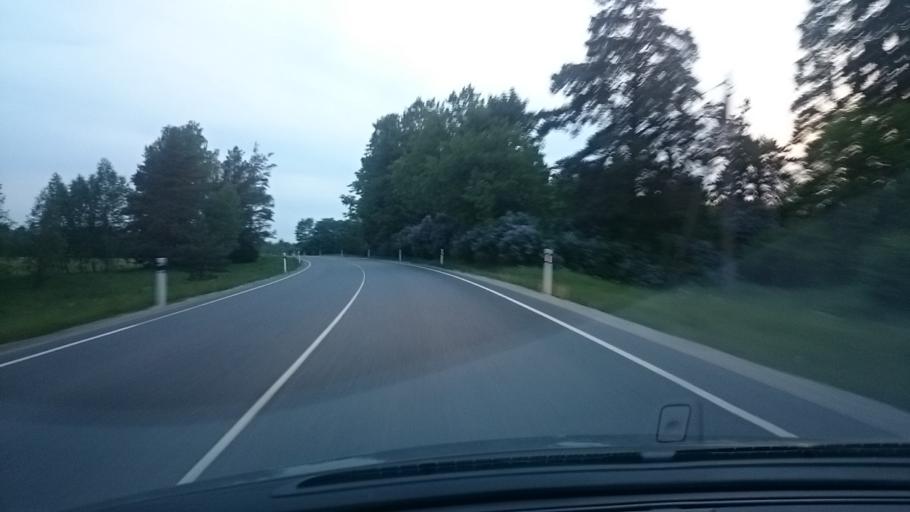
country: EE
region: Raplamaa
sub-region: Kehtna vald
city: Kehtna
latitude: 58.9008
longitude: 24.8977
